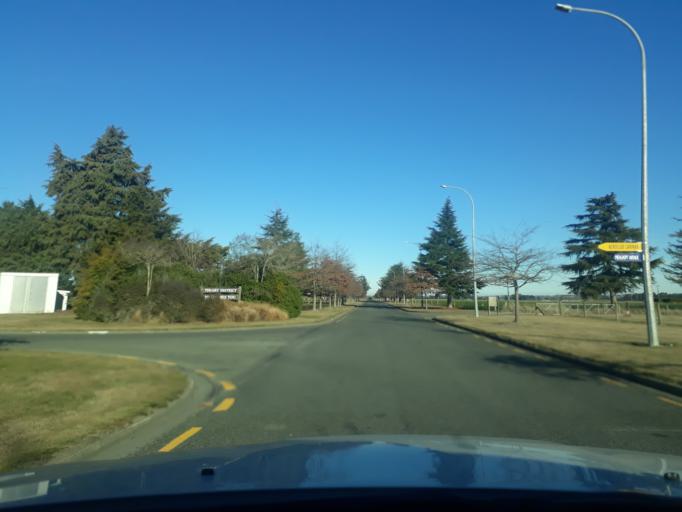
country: NZ
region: Canterbury
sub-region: Timaru District
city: Timaru
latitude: -44.3039
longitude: 171.2254
